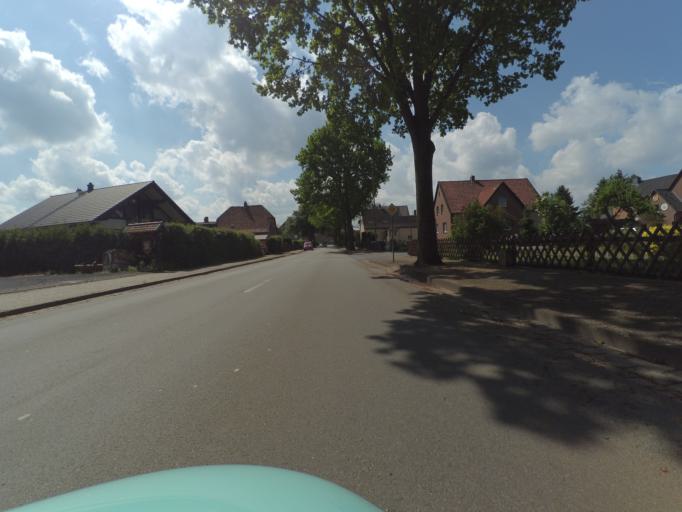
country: DE
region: Lower Saxony
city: Vechelde
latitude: 52.3081
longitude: 10.3152
